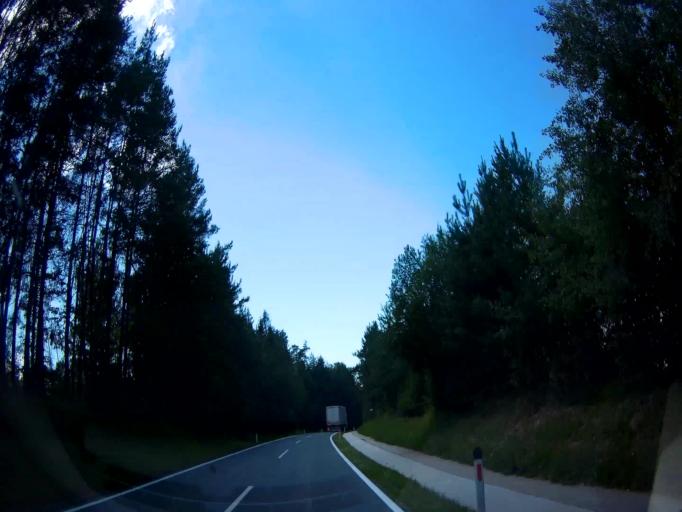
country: AT
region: Carinthia
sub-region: Politischer Bezirk Volkermarkt
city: Eberndorf
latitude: 46.6085
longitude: 14.6887
